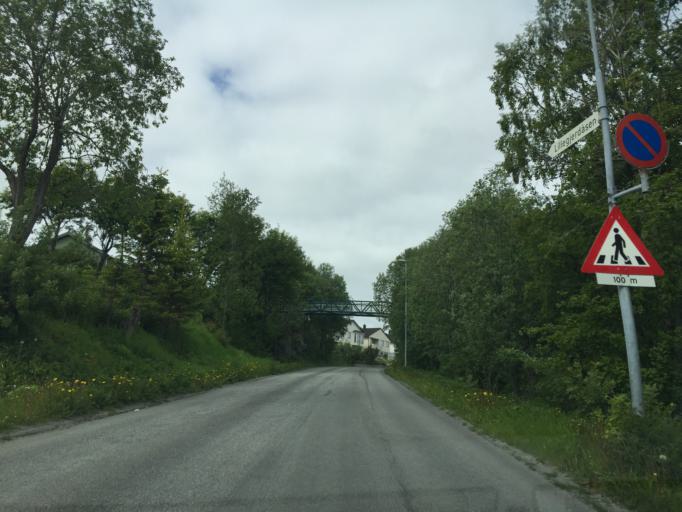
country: NO
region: Nordland
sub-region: Bodo
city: Lopsmarka
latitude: 67.2845
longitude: 14.5522
